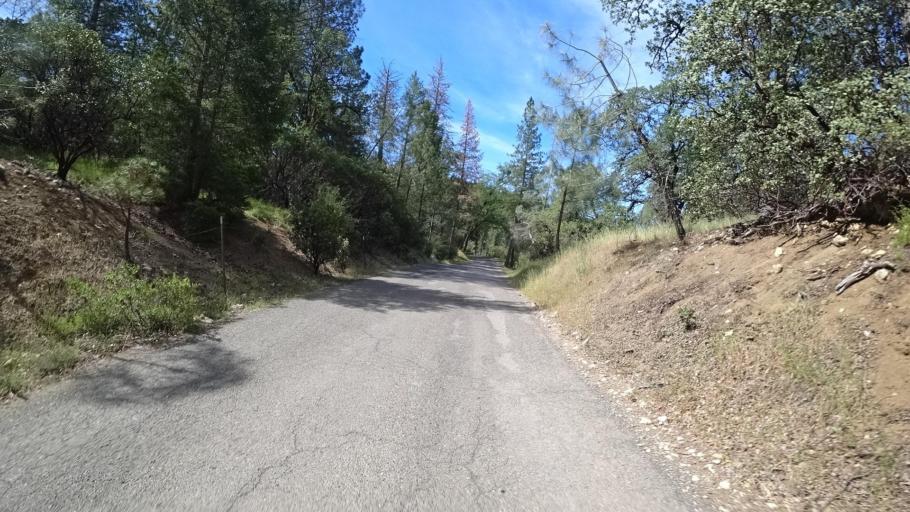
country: US
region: California
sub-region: Lake County
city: Cobb
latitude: 38.8614
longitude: -122.7417
